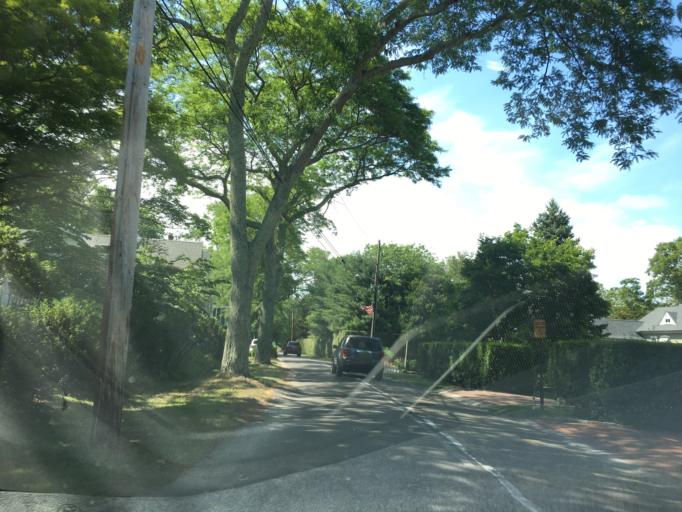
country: US
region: New York
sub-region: Suffolk County
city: Shelter Island Heights
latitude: 41.0850
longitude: -72.3545
